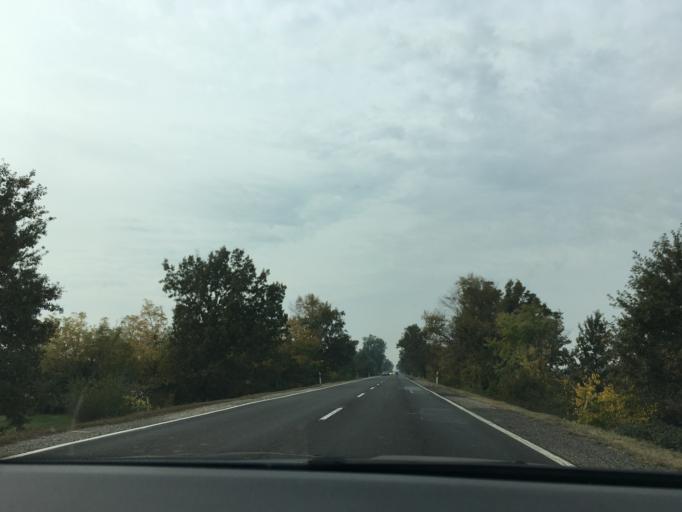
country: HU
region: Hajdu-Bihar
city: Debrecen
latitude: 47.5002
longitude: 21.5719
